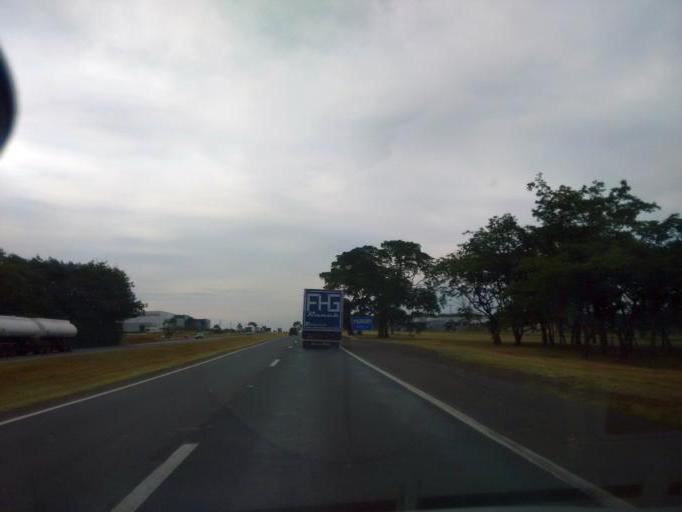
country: BR
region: Sao Paulo
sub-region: Araraquara
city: Araraquara
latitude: -21.7886
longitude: -48.2183
